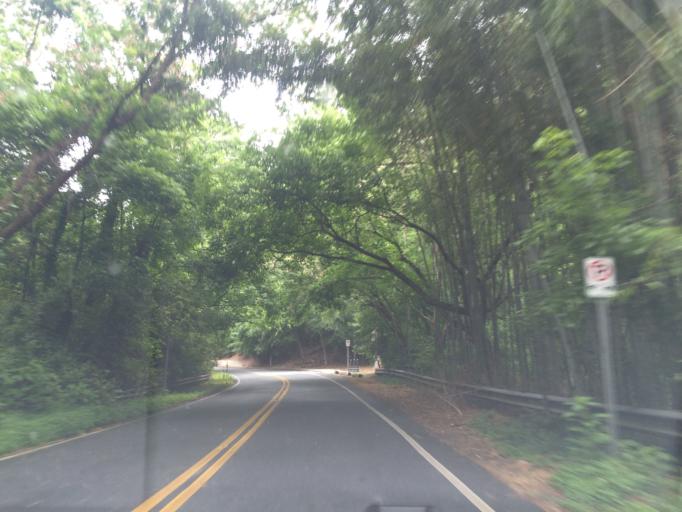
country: US
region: Georgia
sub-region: DeKalb County
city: Druid Hills
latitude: 33.8008
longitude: -84.3350
